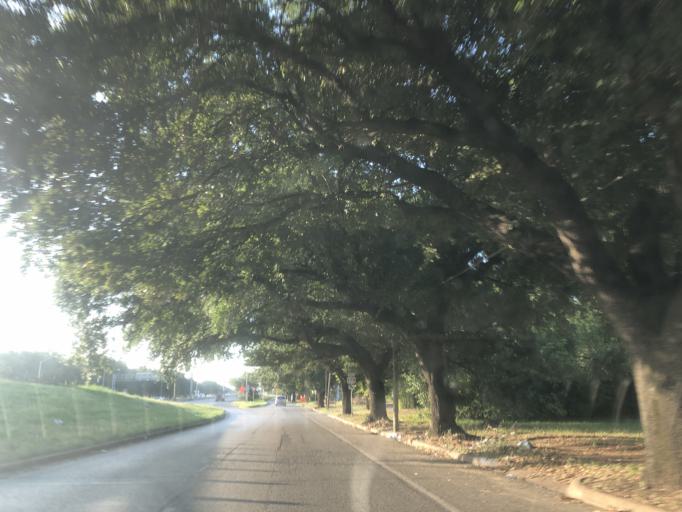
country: US
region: Texas
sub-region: Dallas County
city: Dallas
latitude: 32.7570
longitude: -96.7680
